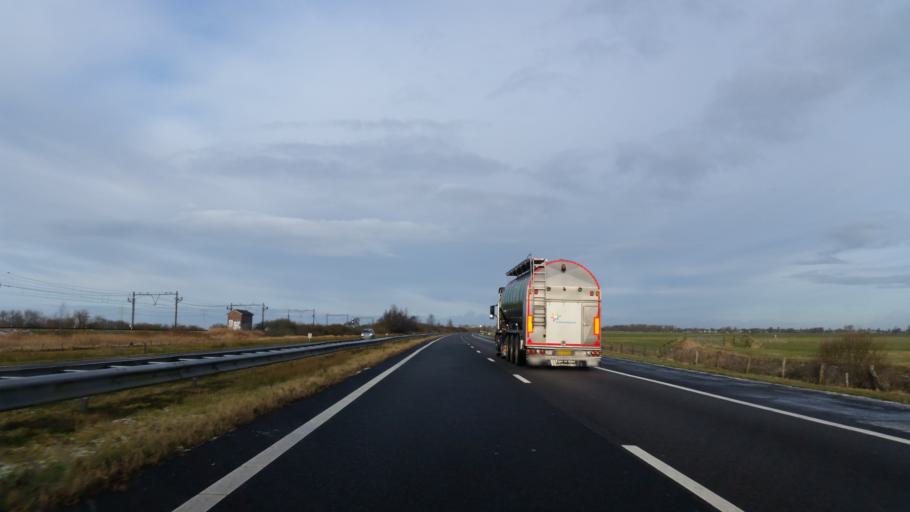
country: NL
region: Friesland
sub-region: Gemeente Boarnsterhim
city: Akkrum
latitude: 53.0637
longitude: 5.8365
